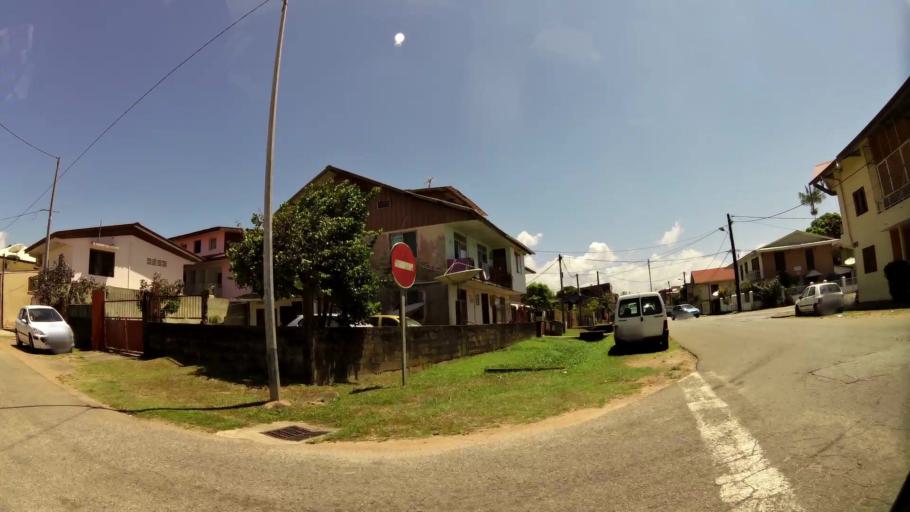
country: GF
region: Guyane
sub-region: Guyane
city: Cayenne
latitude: 4.9319
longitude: -52.3310
